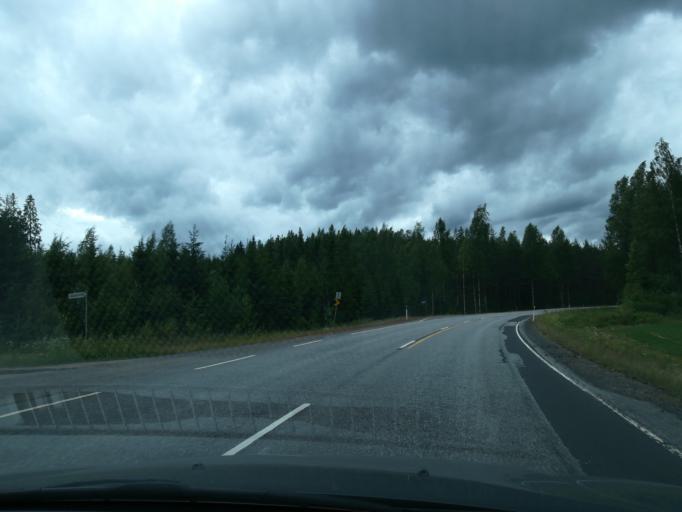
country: FI
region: South Karelia
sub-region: Lappeenranta
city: Lemi
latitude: 61.1133
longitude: 27.8626
